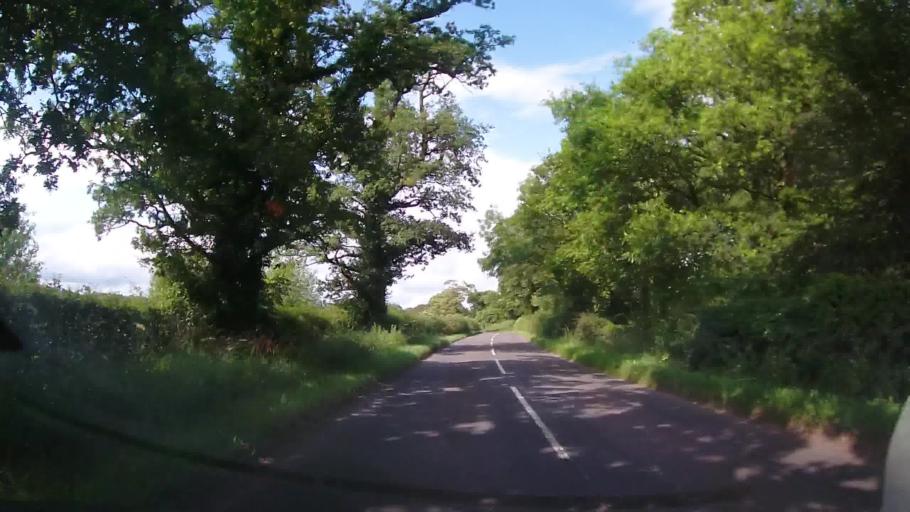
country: GB
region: England
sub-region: Shropshire
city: Petton
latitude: 52.8255
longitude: -2.8102
